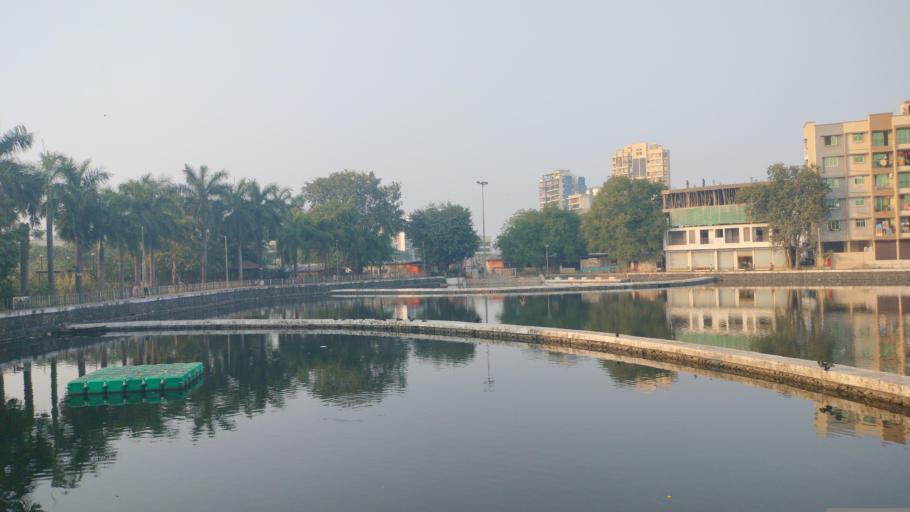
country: IN
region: Maharashtra
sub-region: Thane
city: Airoli
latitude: 19.1272
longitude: 72.9981
